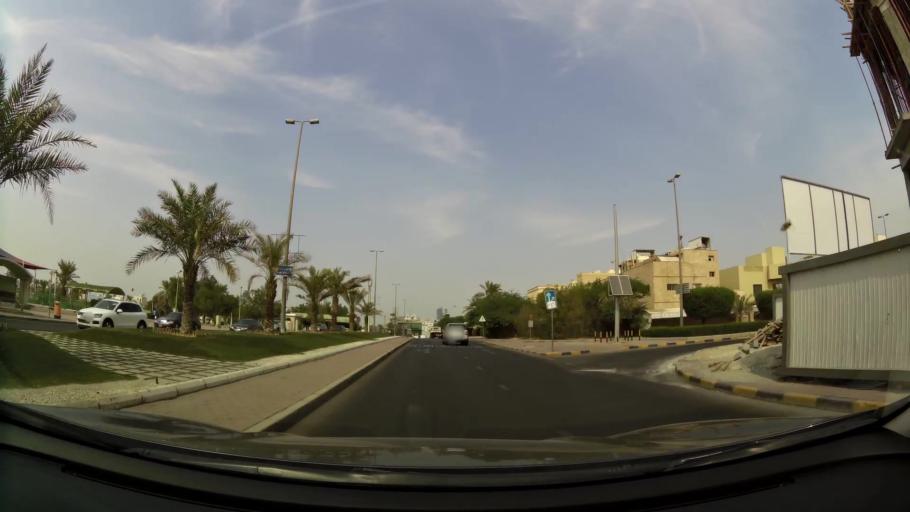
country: KW
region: Al Asimah
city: Ash Shamiyah
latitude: 29.3363
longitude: 47.9620
